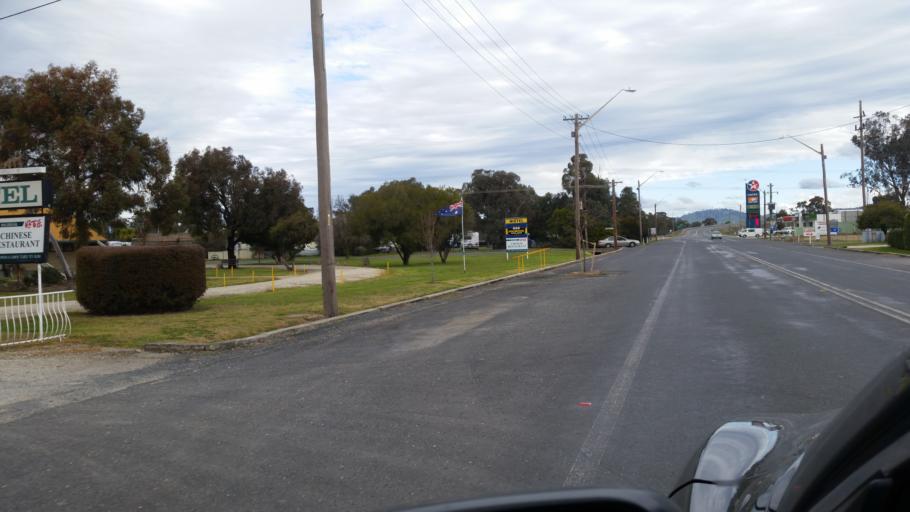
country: AU
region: New South Wales
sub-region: Greater Hume Shire
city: Holbrook
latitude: -35.7287
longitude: 147.3104
